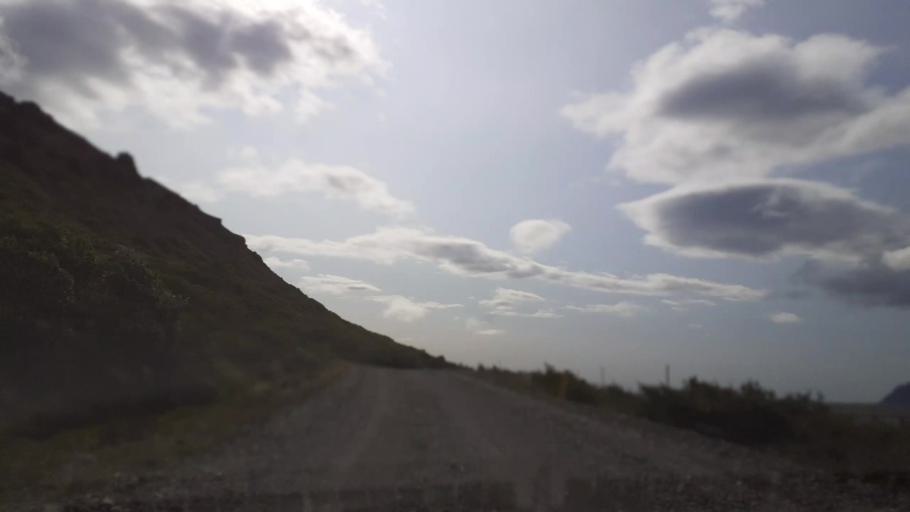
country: IS
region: East
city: Hoefn
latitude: 64.4256
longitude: -14.8827
